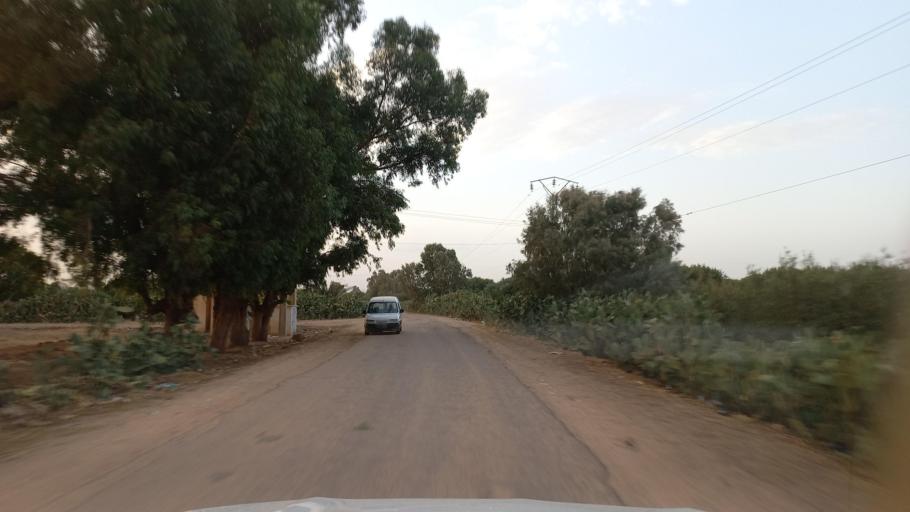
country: TN
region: Al Qasrayn
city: Kasserine
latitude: 35.2671
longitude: 9.0597
